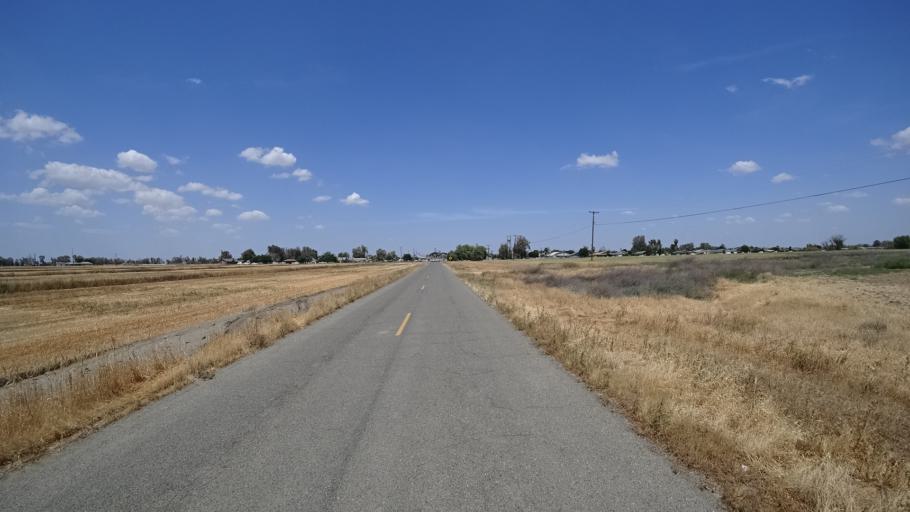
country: US
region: California
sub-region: Kings County
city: Stratford
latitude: 36.1834
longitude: -119.8253
